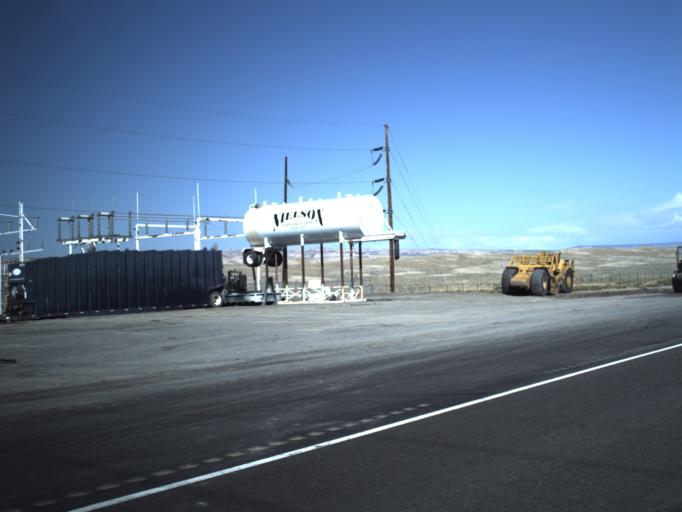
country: US
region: Utah
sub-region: Carbon County
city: East Carbon City
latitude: 39.0259
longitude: -110.2997
